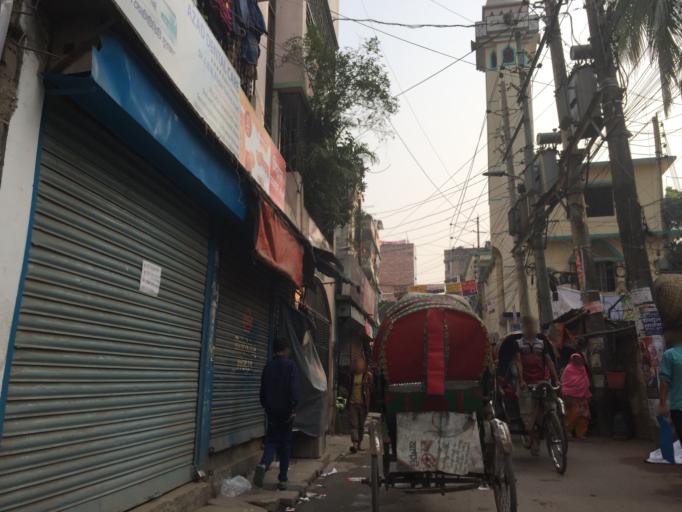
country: BD
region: Dhaka
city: Azimpur
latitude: 23.7260
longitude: 90.3819
